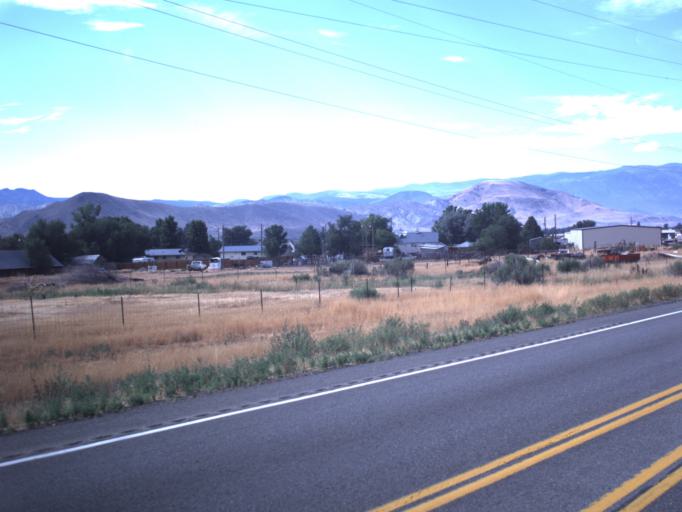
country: US
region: Utah
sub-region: Sevier County
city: Aurora
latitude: 38.8632
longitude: -111.9673
